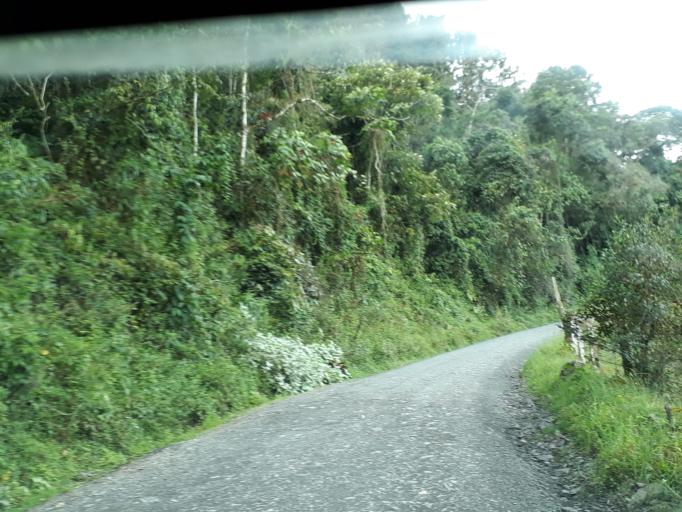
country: CO
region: Cundinamarca
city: Pacho
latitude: 5.2556
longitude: -74.1796
